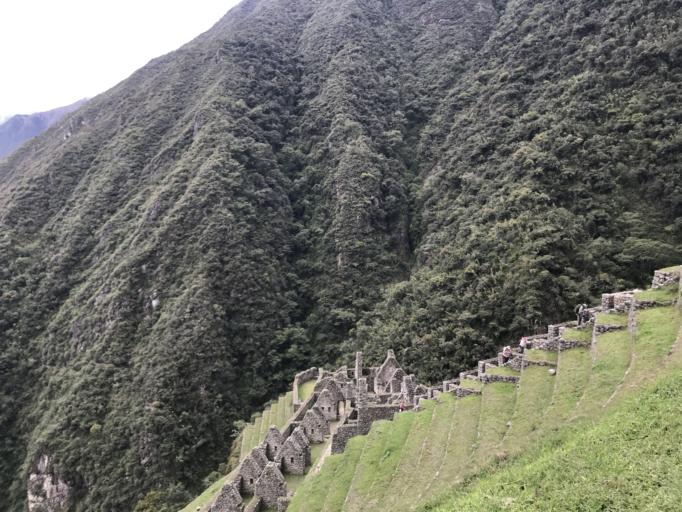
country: PE
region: Cusco
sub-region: Provincia de La Convencion
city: Santa Teresa
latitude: -13.1930
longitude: -72.5369
